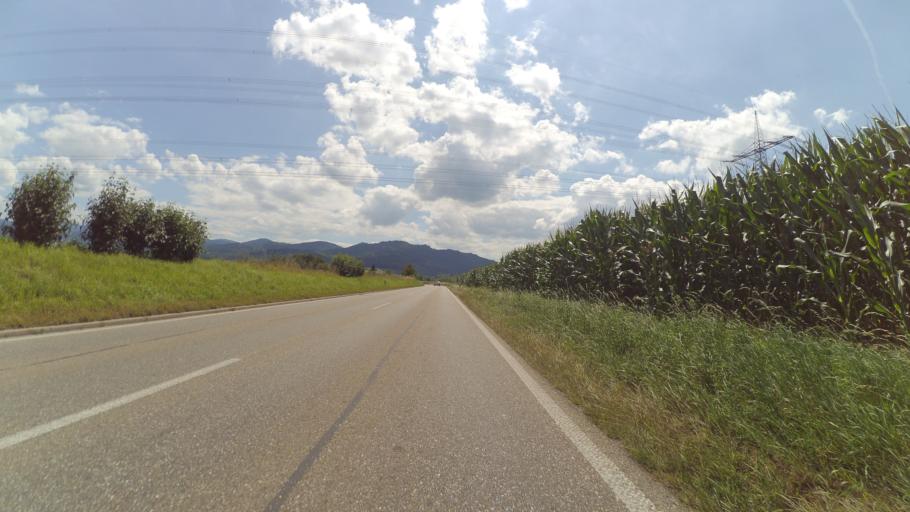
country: DE
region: Baden-Wuerttemberg
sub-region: Freiburg Region
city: Bad Krozingen
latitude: 47.9027
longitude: 7.7164
